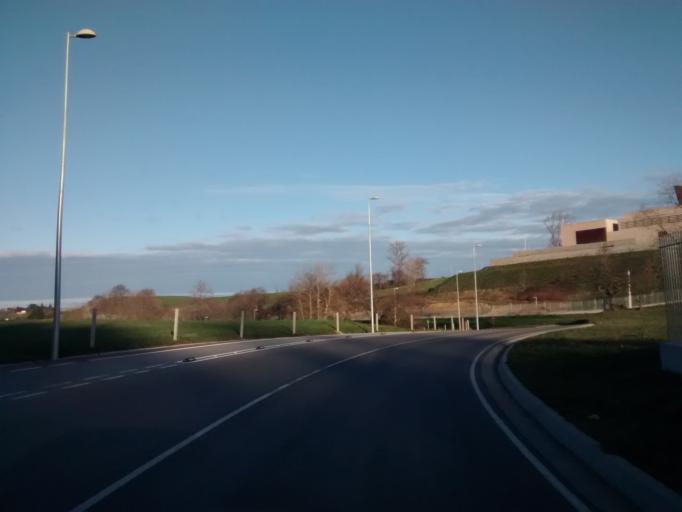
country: ES
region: Cantabria
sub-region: Provincia de Cantabria
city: Lierganes
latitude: 43.3884
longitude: -3.7534
